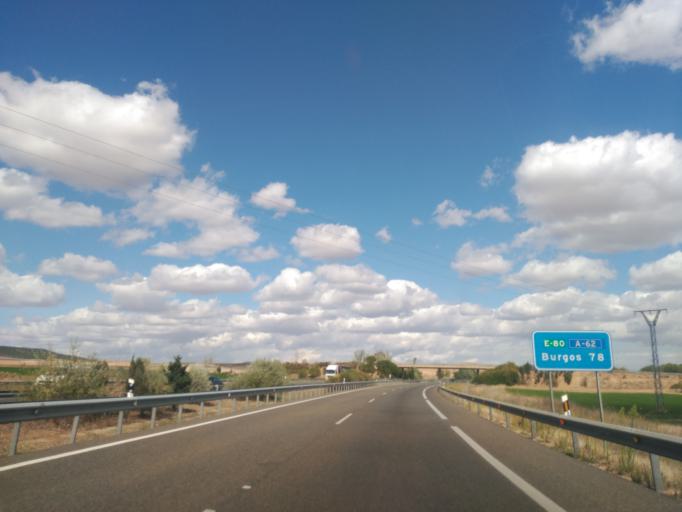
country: ES
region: Castille and Leon
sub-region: Provincia de Palencia
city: Soto de Cerrato
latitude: 41.9850
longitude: -4.4309
